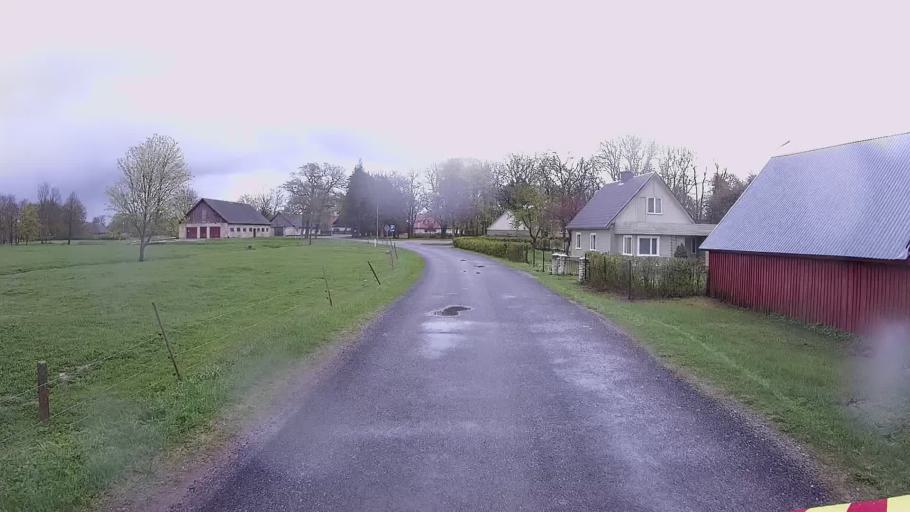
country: EE
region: Hiiumaa
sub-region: Kaerdla linn
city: Kardla
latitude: 58.6974
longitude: 22.5711
